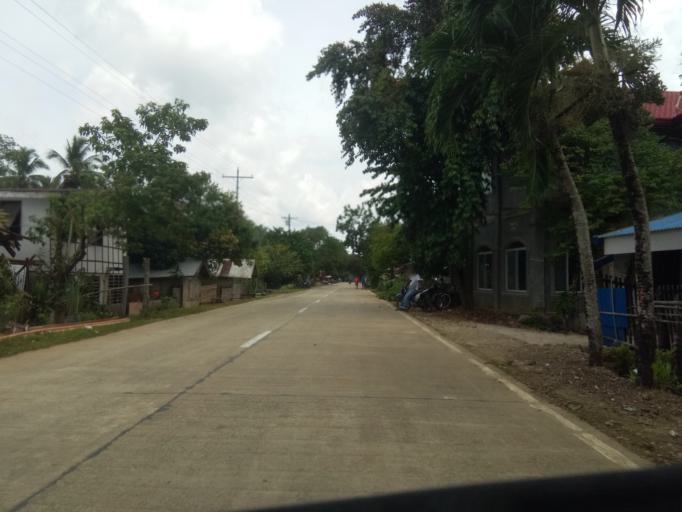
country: PH
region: Caraga
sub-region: Province of Surigao del Norte
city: San Isidro
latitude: 9.9283
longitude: 126.0569
